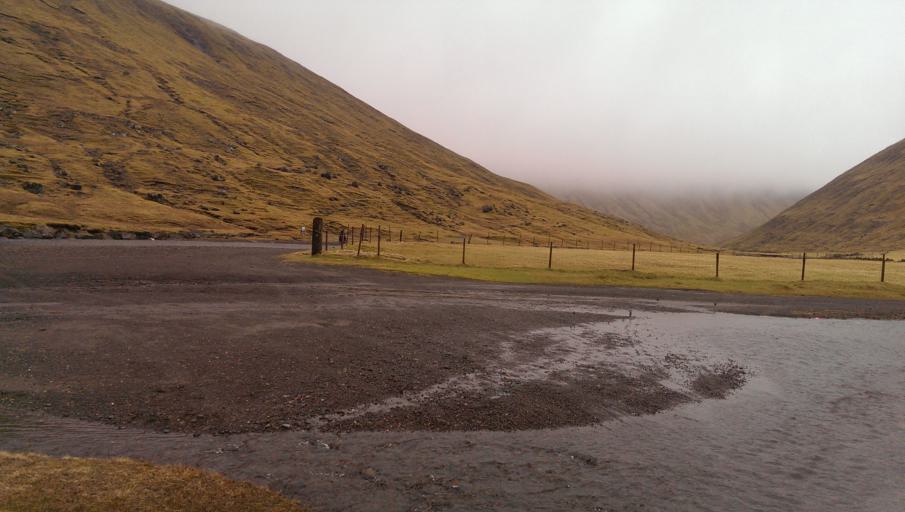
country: FO
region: Streymoy
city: Kollafjordhur
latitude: 62.1323
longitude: -7.0229
